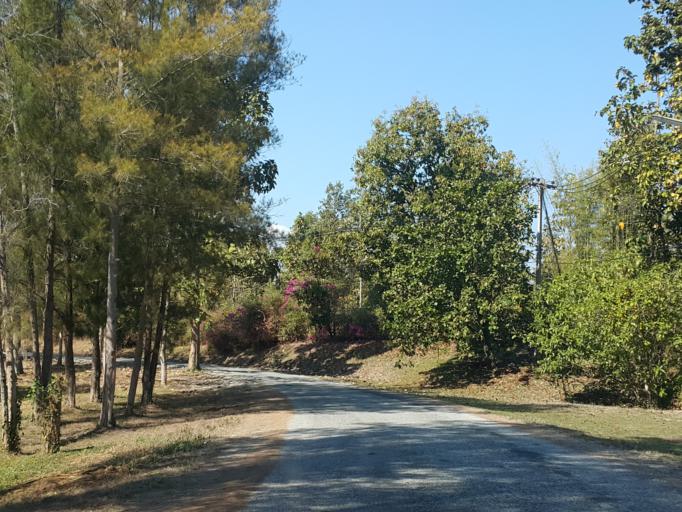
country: TH
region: Chiang Mai
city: Mae Taeng
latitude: 19.0299
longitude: 98.9924
